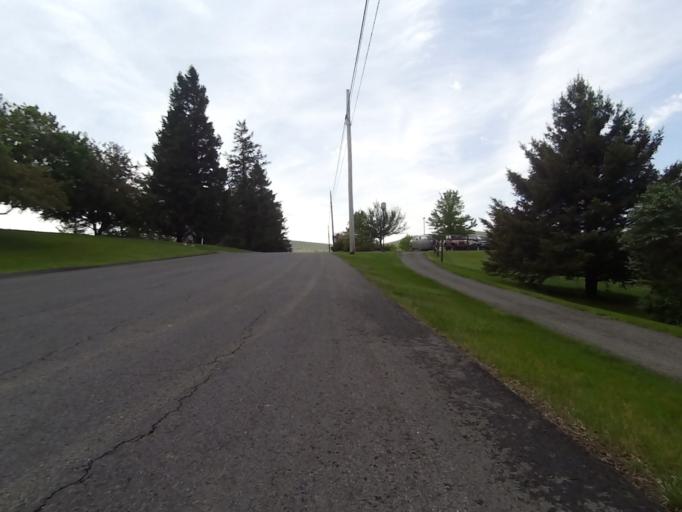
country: US
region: Pennsylvania
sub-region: Centre County
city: Boalsburg
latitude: 40.7862
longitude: -77.7587
